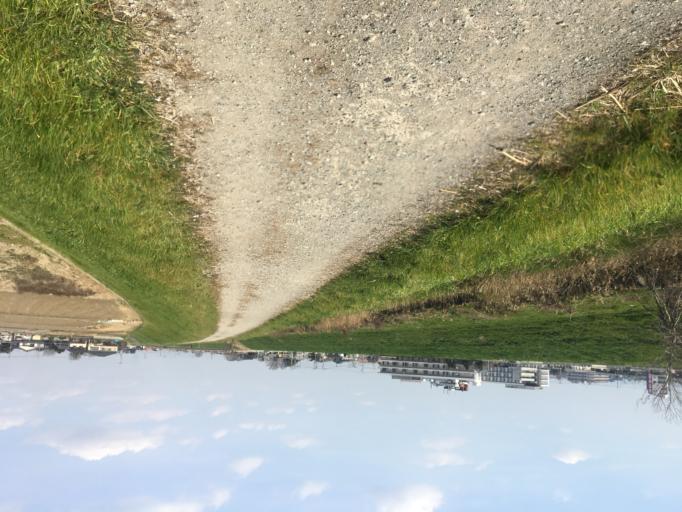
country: JP
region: Saitama
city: Kamifukuoka
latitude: 35.8753
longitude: 139.5449
